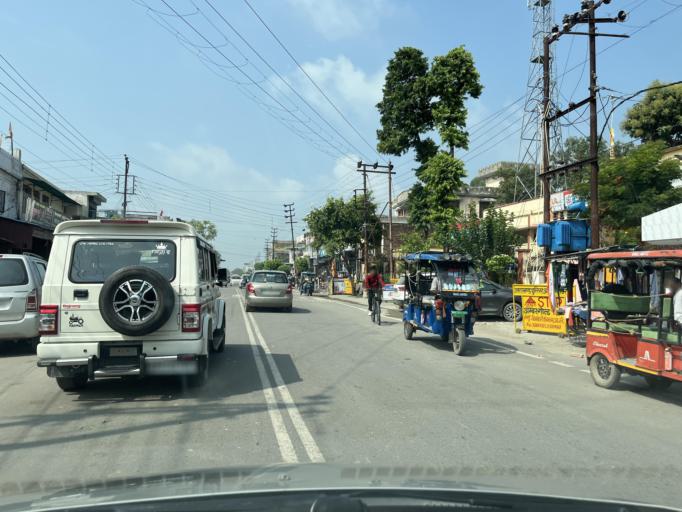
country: IN
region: Uttarakhand
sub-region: Udham Singh Nagar
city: Bazpur
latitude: 29.1619
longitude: 79.1549
